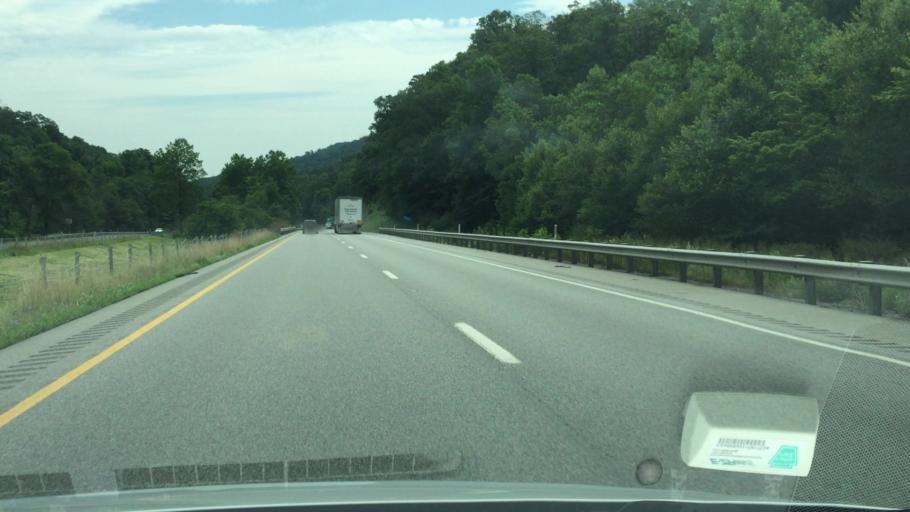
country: US
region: Maryland
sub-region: Washington County
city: Hancock
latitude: 39.8016
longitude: -78.2575
